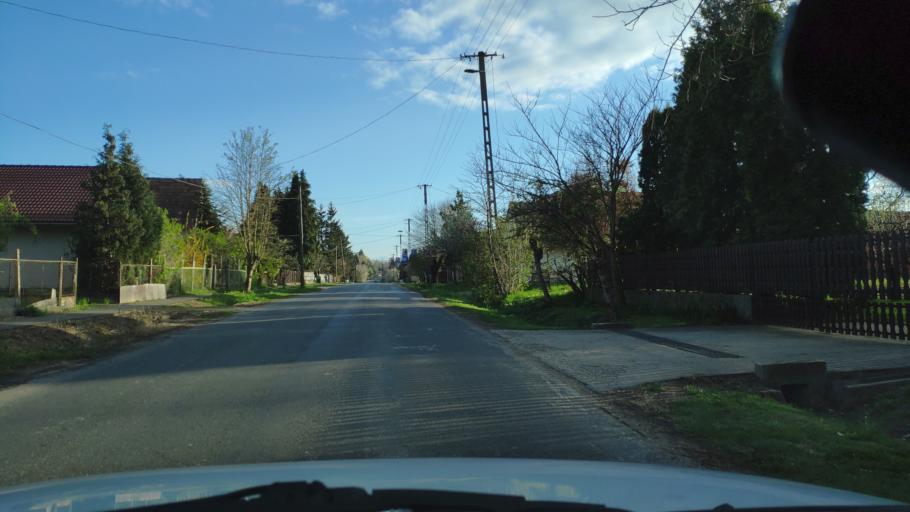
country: HU
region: Zala
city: Zalakomar
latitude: 46.4558
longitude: 17.1261
